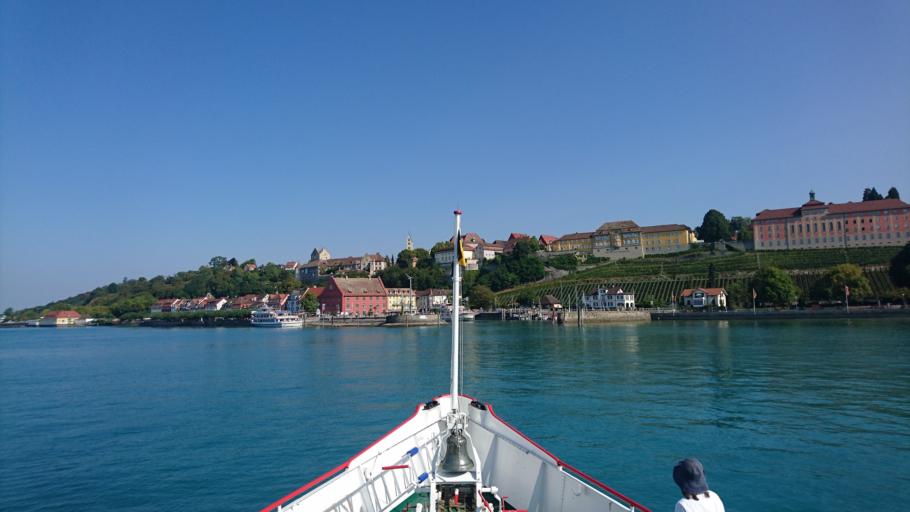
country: DE
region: Baden-Wuerttemberg
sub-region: Tuebingen Region
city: Meersburg
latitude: 47.6898
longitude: 9.2732
